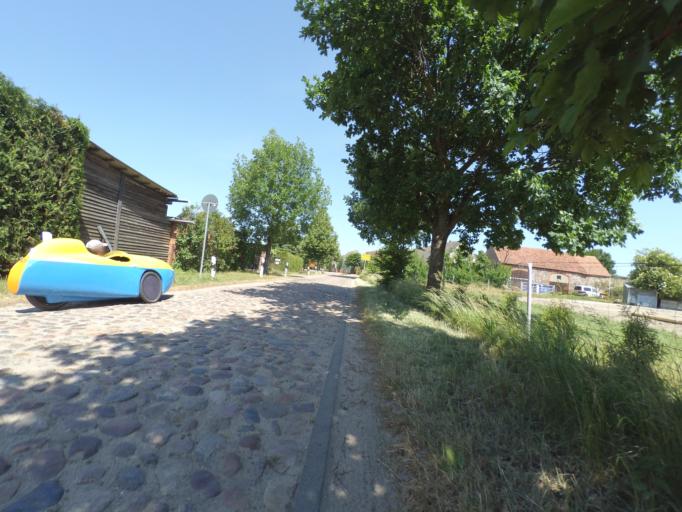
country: DE
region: Brandenburg
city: Gerdshagen
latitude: 53.2780
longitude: 12.2829
